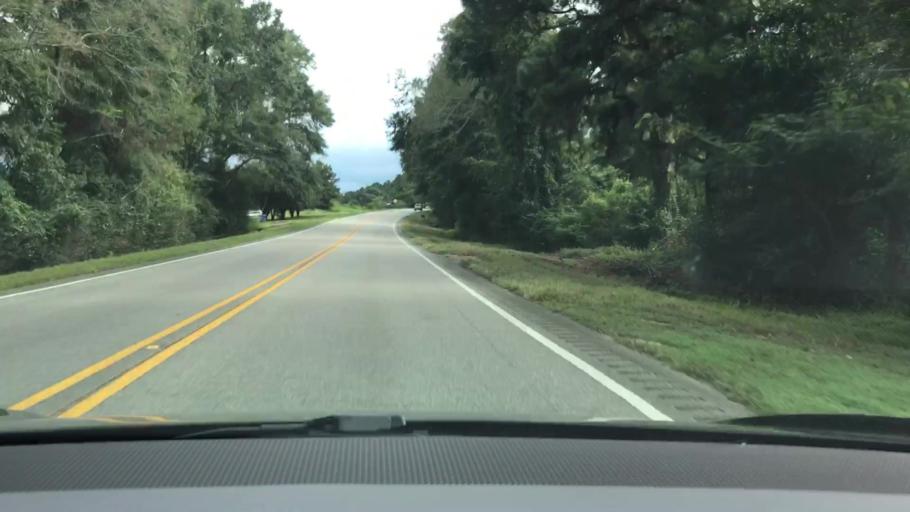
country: US
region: Alabama
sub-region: Coffee County
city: Elba
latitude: 31.5584
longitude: -86.0138
